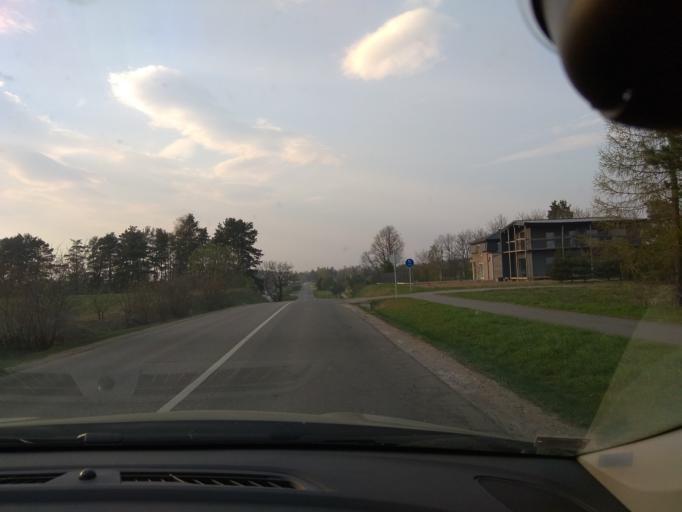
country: LT
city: Grigiskes
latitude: 54.6192
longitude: 25.1151
